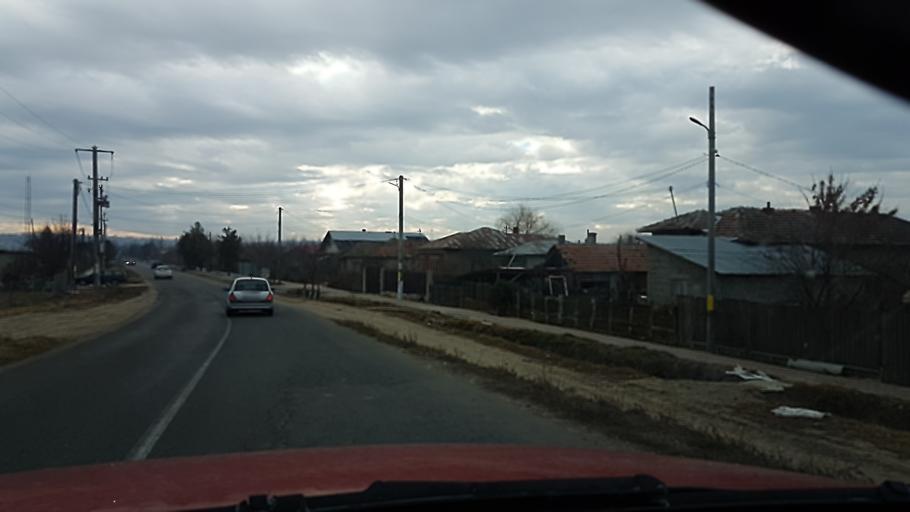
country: RO
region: Giurgiu
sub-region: Comuna Hotarele
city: Hotarele
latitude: 44.1880
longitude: 26.3658
